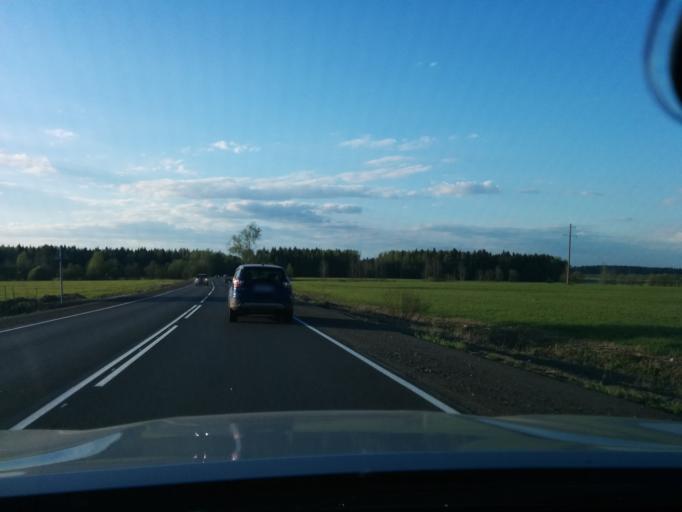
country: RU
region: Leningrad
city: Verkhniye Osel'ki
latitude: 60.2009
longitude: 30.4265
